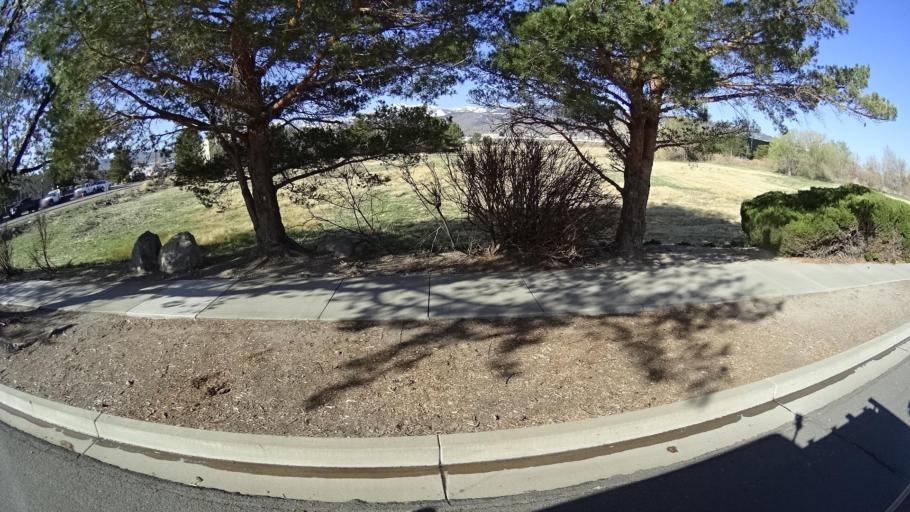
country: US
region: Nevada
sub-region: Washoe County
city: Sparks
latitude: 39.4450
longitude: -119.7639
